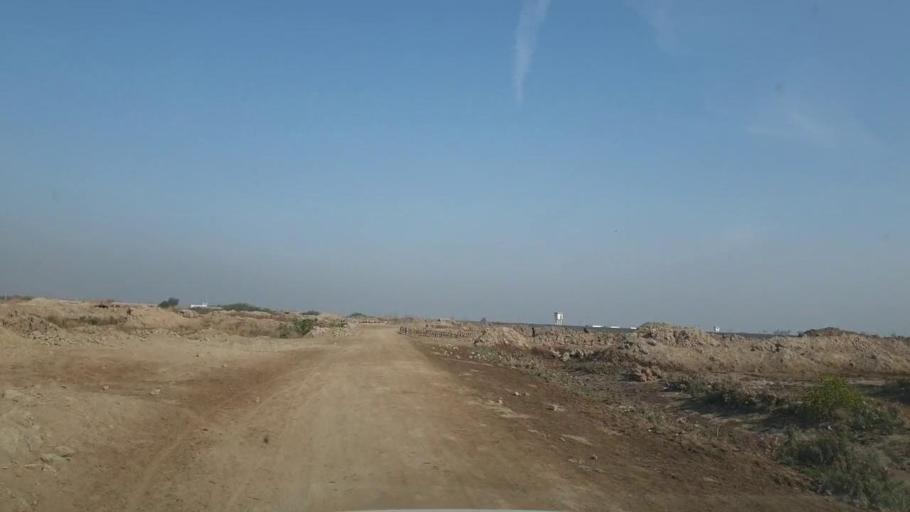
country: PK
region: Sindh
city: Mirpur Khas
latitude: 25.5189
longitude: 69.0679
